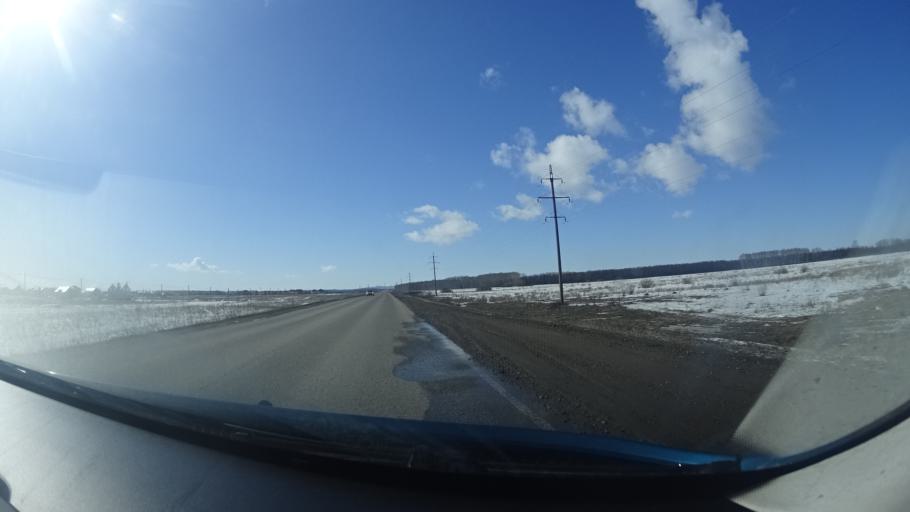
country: RU
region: Bashkortostan
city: Ufa
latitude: 54.6334
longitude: 55.9090
